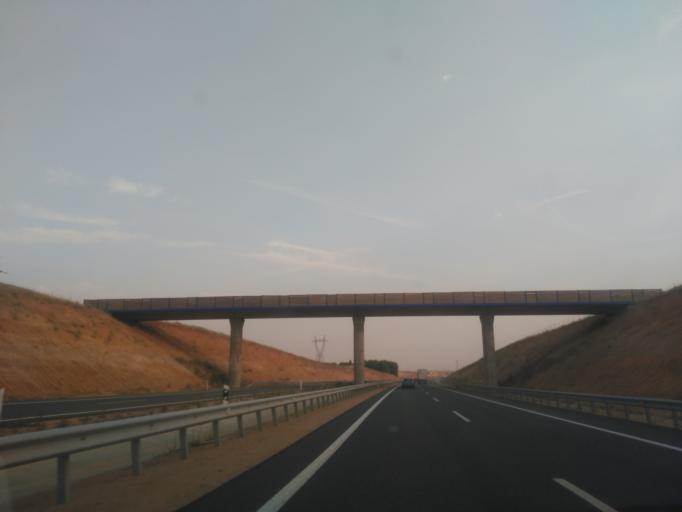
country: ES
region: Castille and Leon
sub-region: Provincia de Zamora
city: Montamarta
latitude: 41.6590
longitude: -5.7968
